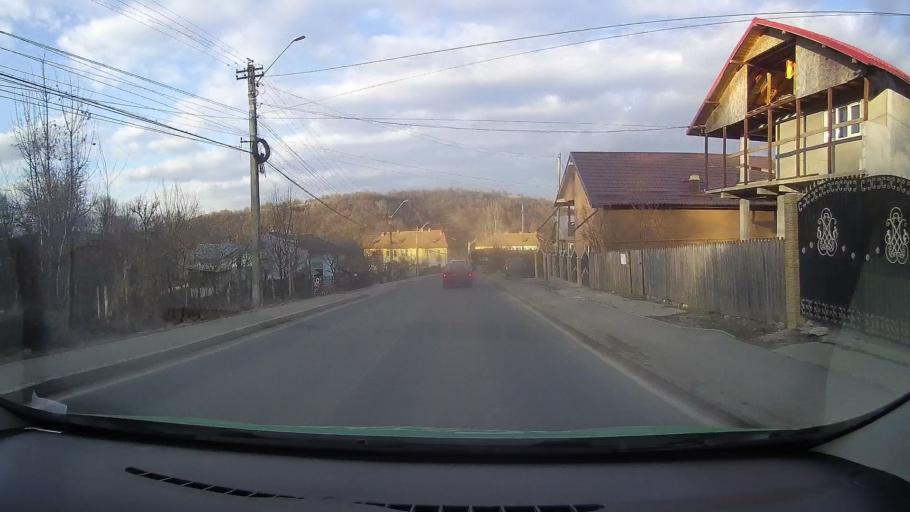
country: RO
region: Dambovita
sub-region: Municipiul Moreni
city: Moreni
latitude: 44.9739
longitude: 25.6166
